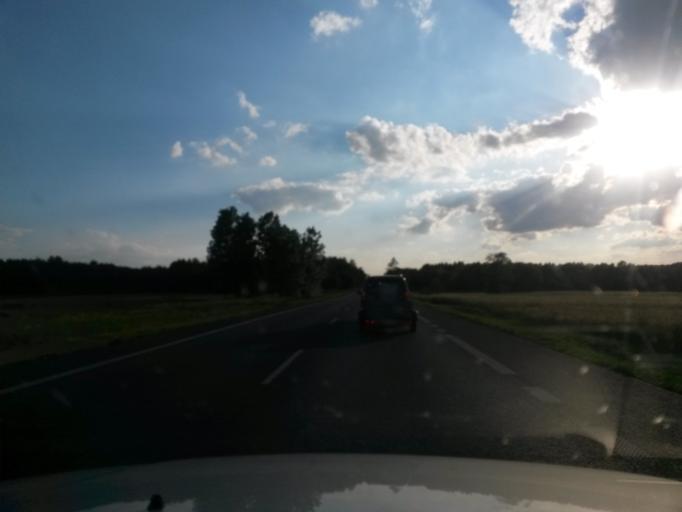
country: PL
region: Lodz Voivodeship
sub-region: Powiat belchatowski
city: Rusiec
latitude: 51.3139
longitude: 18.9203
